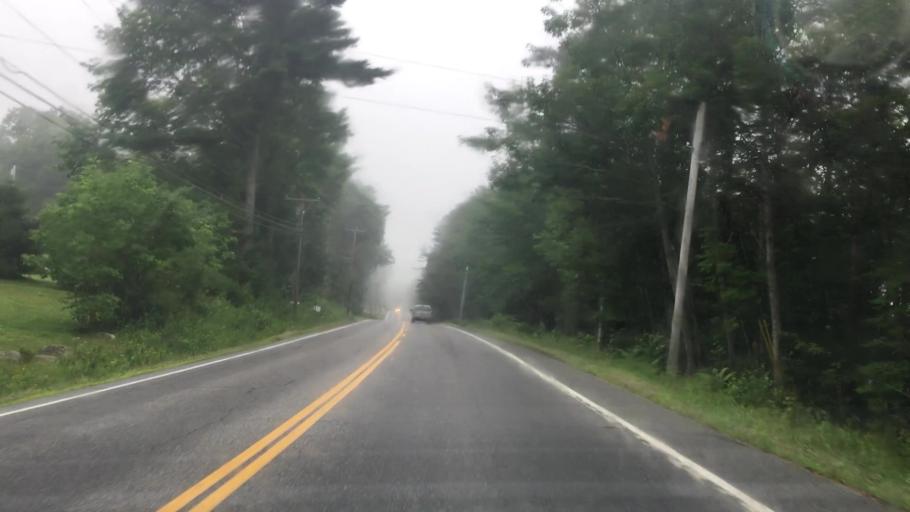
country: US
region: Maine
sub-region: Lincoln County
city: Boothbay
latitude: 43.8932
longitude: -69.6287
